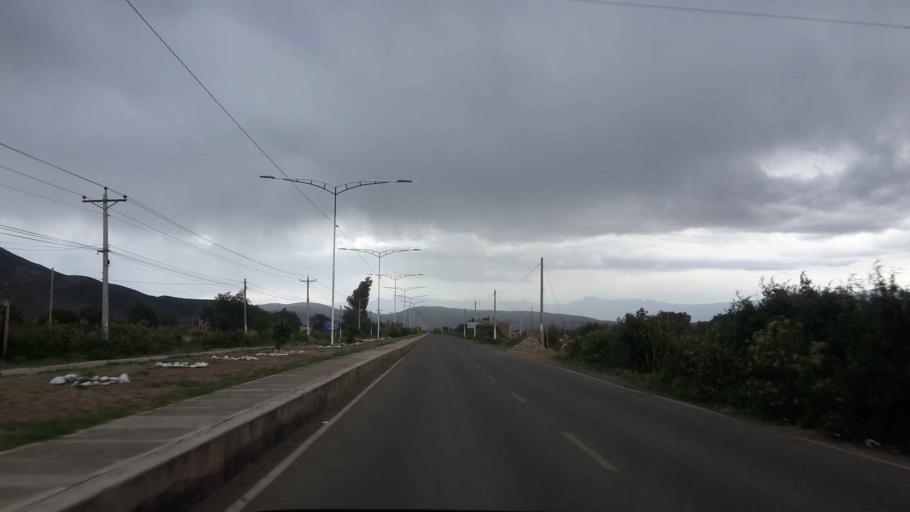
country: BO
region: Cochabamba
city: Tarata
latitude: -17.5977
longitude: -66.0385
